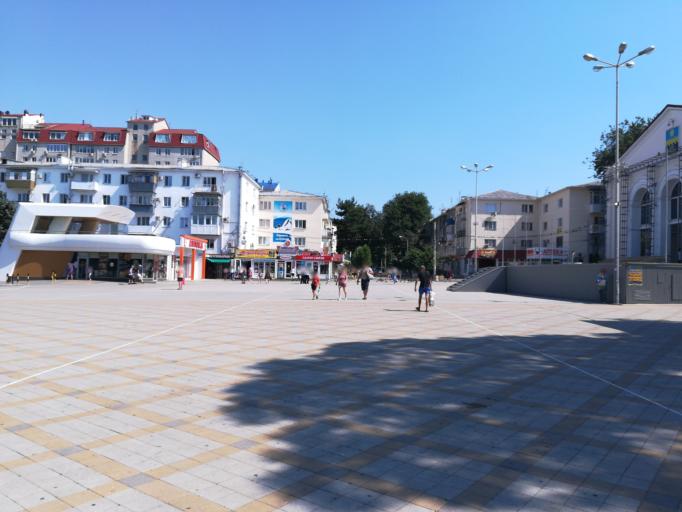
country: RU
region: Krasnodarskiy
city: Anapa
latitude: 44.8943
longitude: 37.3115
